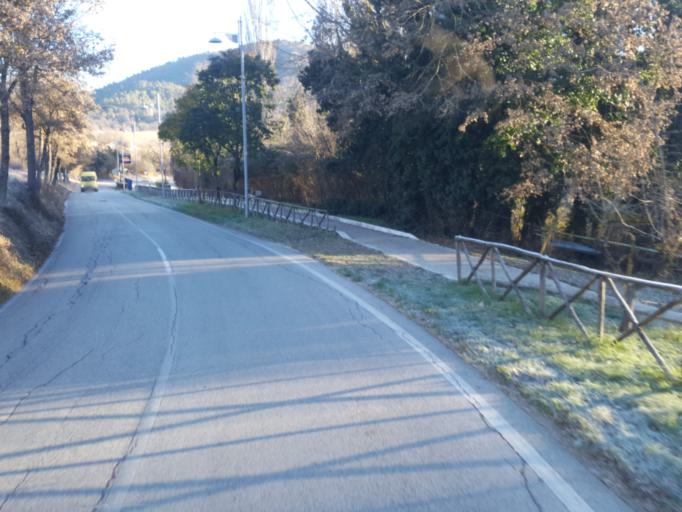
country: IT
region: Latium
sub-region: Provincia di Rieti
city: Labro
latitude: 42.5350
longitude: 12.7659
